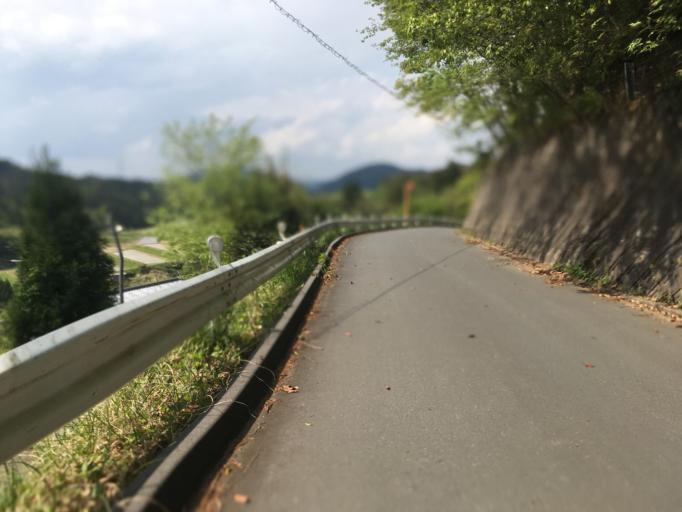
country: JP
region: Kyoto
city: Kameoka
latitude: 35.0708
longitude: 135.6111
